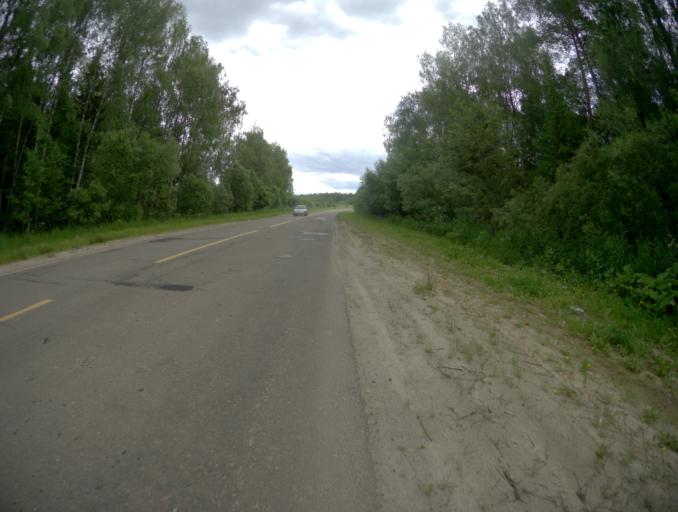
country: RU
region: Ivanovo
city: Kolobovo
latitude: 56.6339
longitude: 41.3673
